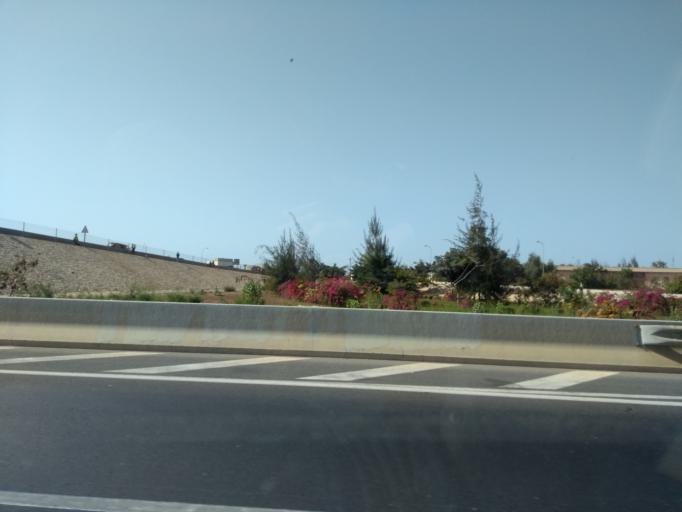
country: SN
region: Dakar
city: Pikine
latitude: 14.7501
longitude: -17.3766
